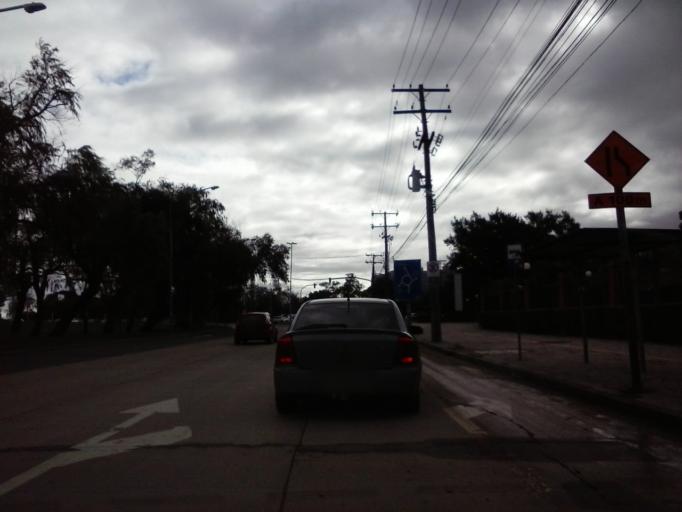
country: BR
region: Rio Grande do Sul
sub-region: Porto Alegre
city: Porto Alegre
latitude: -30.0425
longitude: -51.2320
